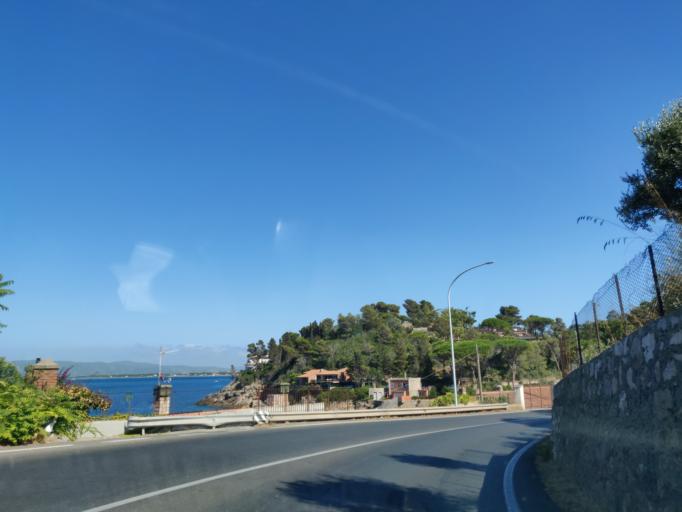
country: IT
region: Tuscany
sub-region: Provincia di Grosseto
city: Monte Argentario
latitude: 42.4378
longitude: 11.1335
